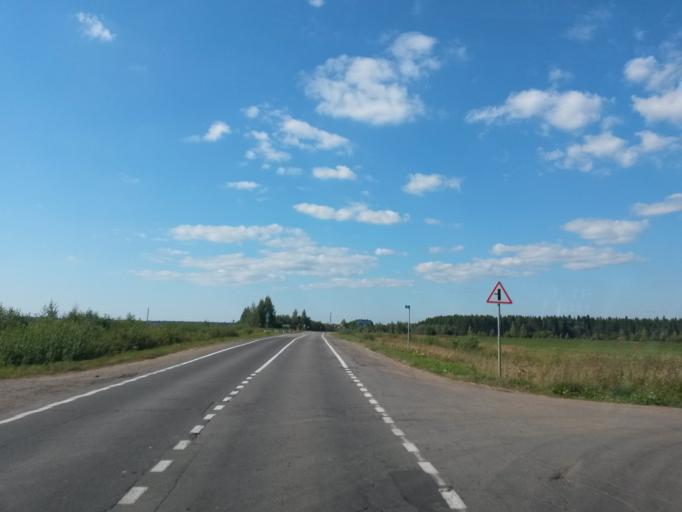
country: RU
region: Jaroslavl
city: Yaroslavl
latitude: 57.7891
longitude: 39.8330
